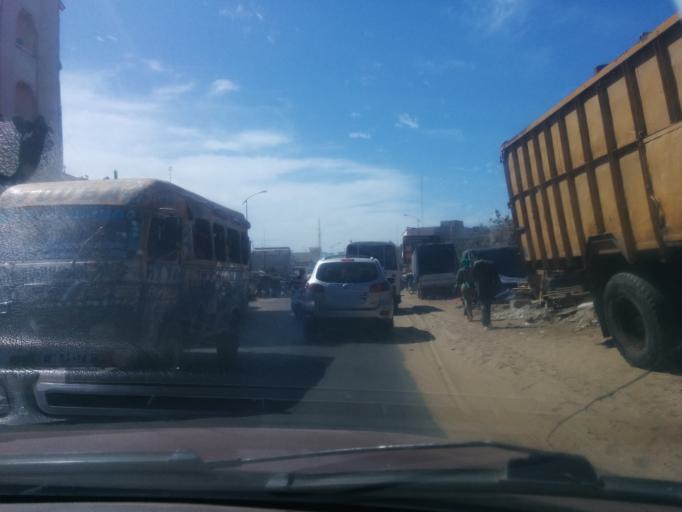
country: SN
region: Dakar
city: Pikine
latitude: 14.7670
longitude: -17.4141
